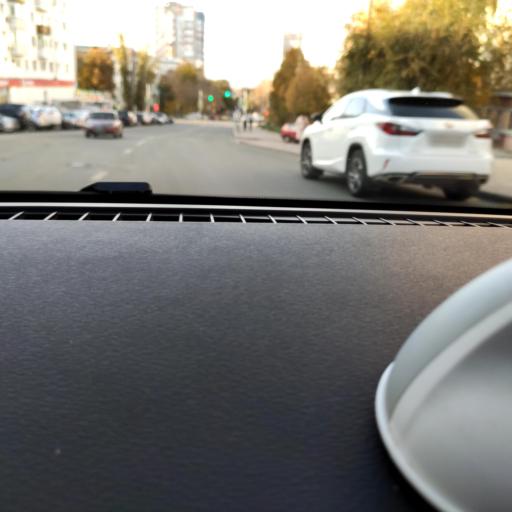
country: RU
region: Samara
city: Samara
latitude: 53.2077
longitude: 50.1255
